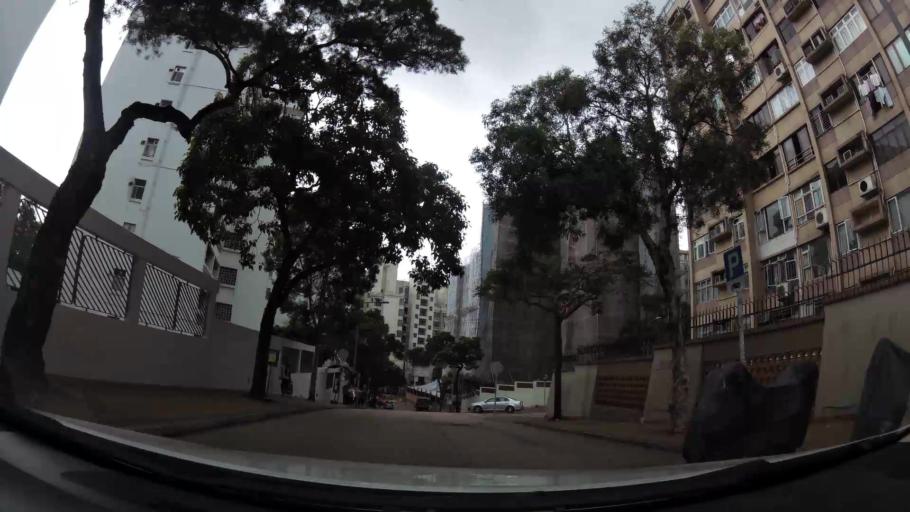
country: HK
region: Wong Tai Sin
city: Wong Tai Sin
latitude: 22.3413
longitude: 114.1830
